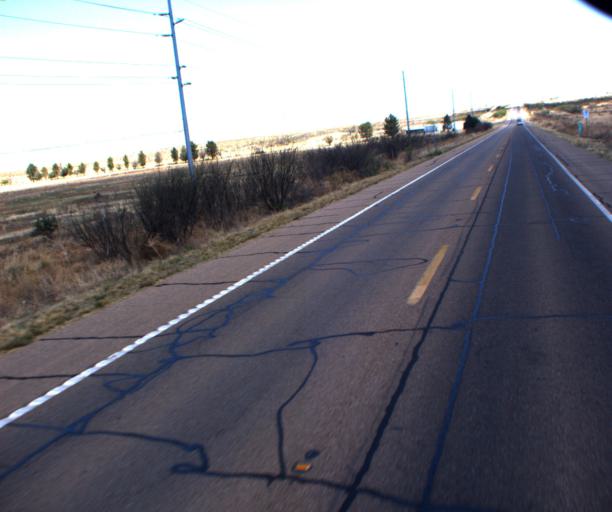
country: US
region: Arizona
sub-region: Cochise County
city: Sierra Vista Southeast
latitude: 31.3800
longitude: -110.1045
